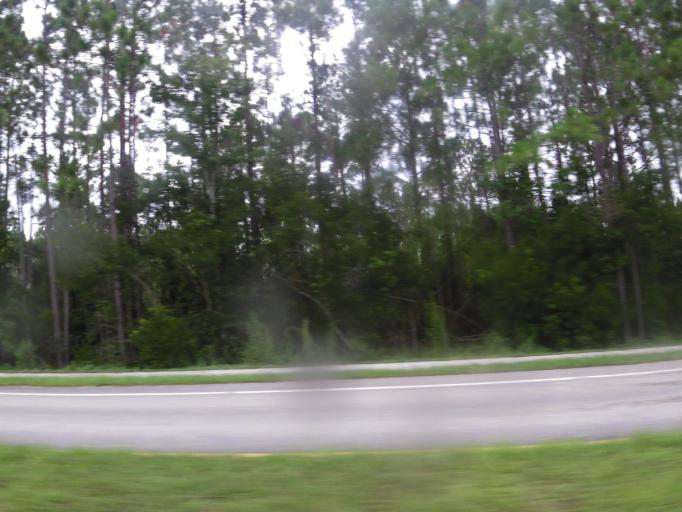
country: US
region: Florida
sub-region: Duval County
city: Jacksonville Beach
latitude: 30.2645
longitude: -81.4488
